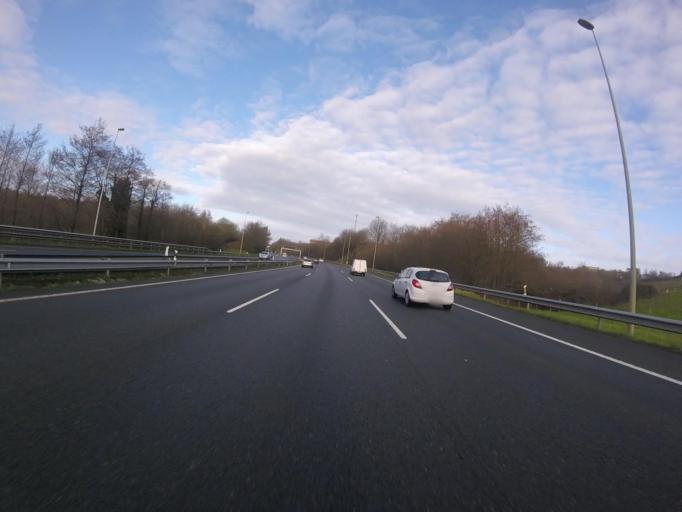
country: ES
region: Basque Country
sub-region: Provincia de Guipuzcoa
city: Pasaia
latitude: 43.3098
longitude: -1.9309
